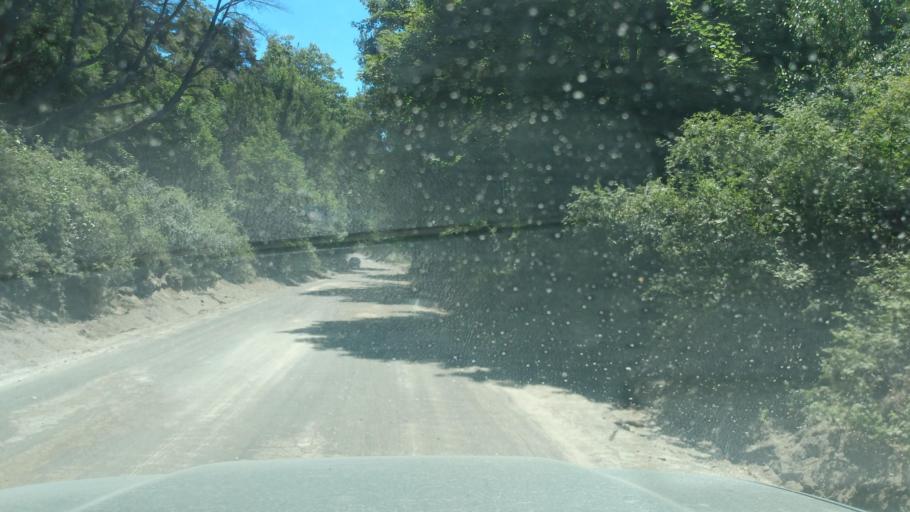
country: AR
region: Neuquen
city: Villa La Angostura
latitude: -40.6288
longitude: -71.4787
